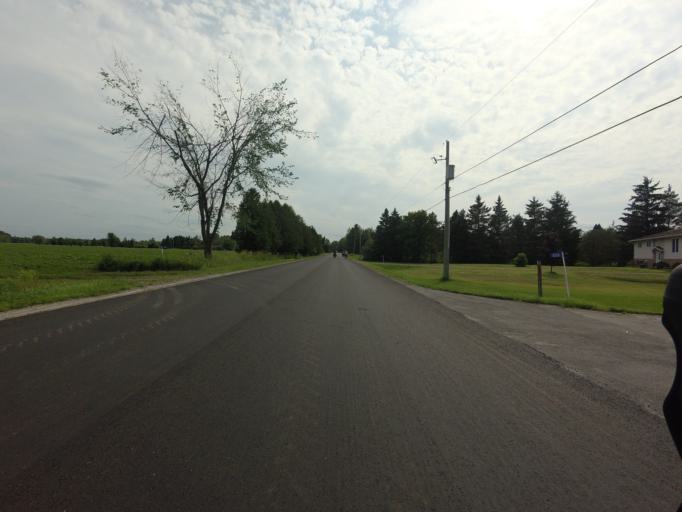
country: CA
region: Ontario
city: Bells Corners
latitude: 45.0605
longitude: -75.6086
